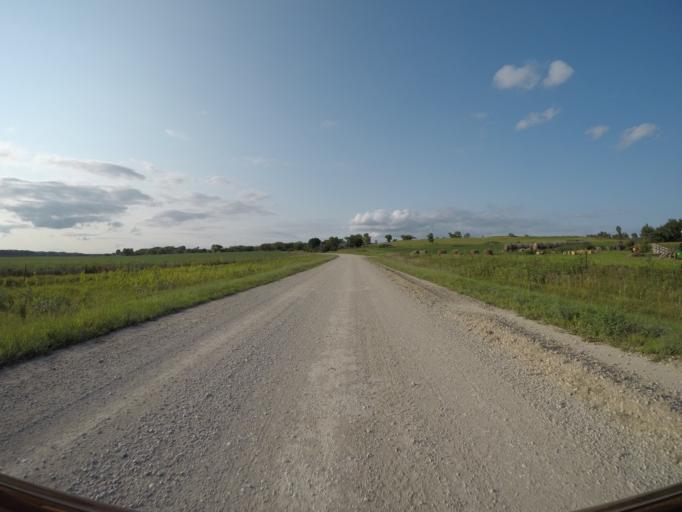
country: US
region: Kansas
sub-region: Wabaunsee County
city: Alma
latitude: 38.9608
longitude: -96.2520
